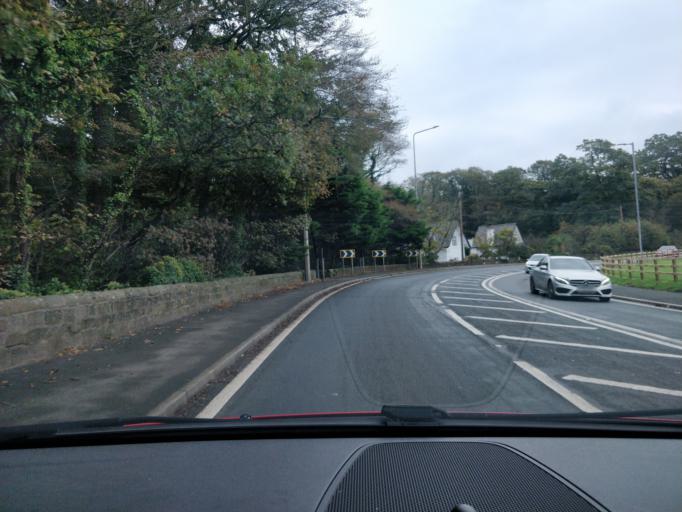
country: GB
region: England
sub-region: Lancashire
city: Ormskirk
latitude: 53.6012
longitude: -2.9272
